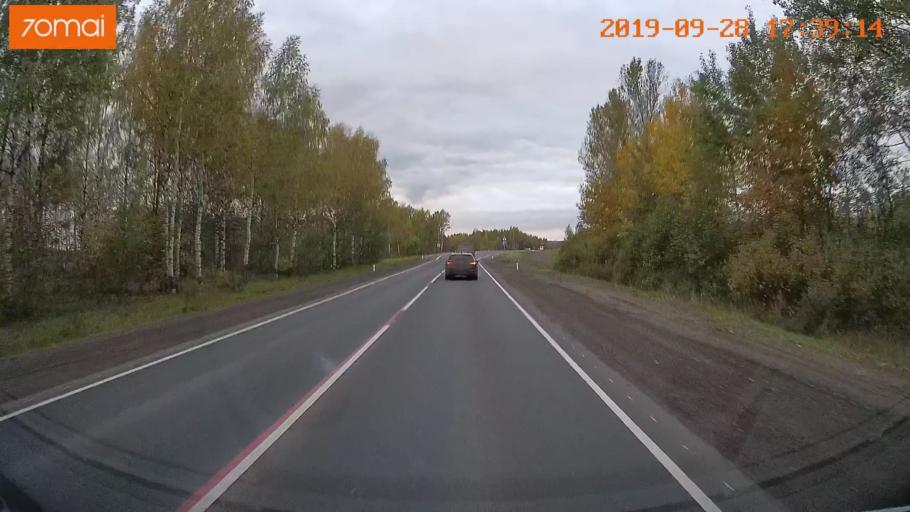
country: RU
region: Jaroslavl
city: Yaroslavl
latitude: 57.5441
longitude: 39.9251
